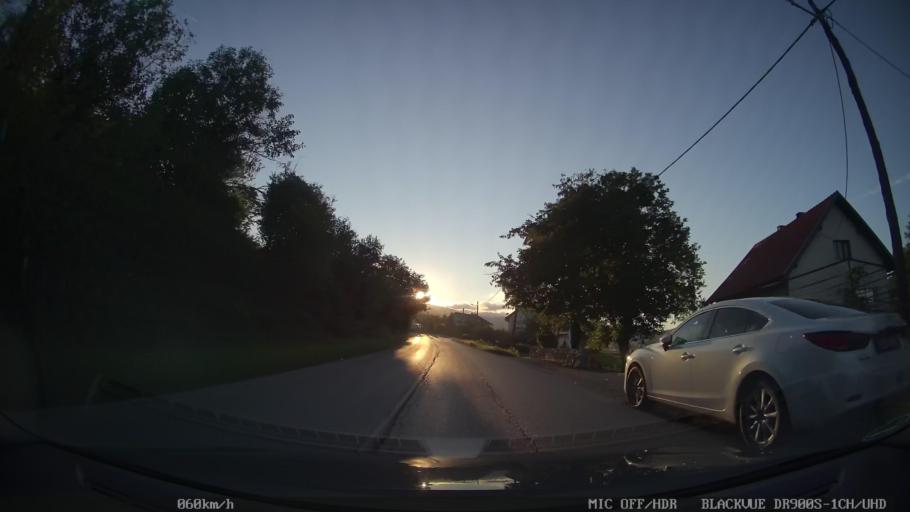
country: HR
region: Karlovacka
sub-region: Grad Ogulin
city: Ogulin
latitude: 45.2687
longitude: 15.1949
